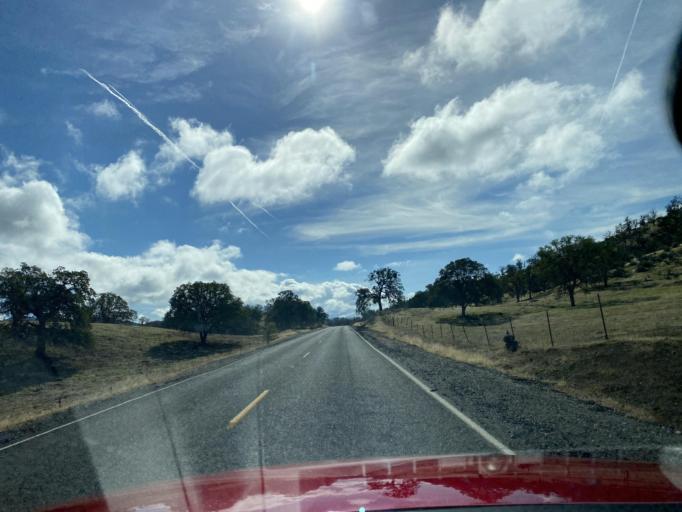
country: US
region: California
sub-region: Glenn County
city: Willows
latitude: 39.4897
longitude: -122.5198
